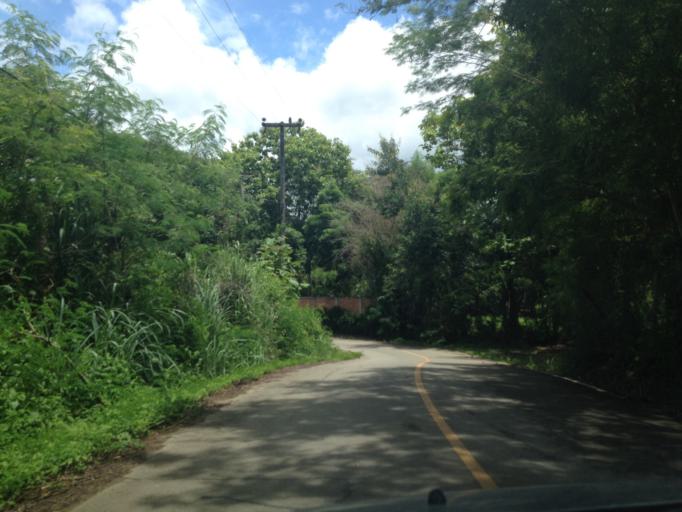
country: TH
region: Chiang Mai
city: Hang Dong
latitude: 18.7225
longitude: 98.8847
